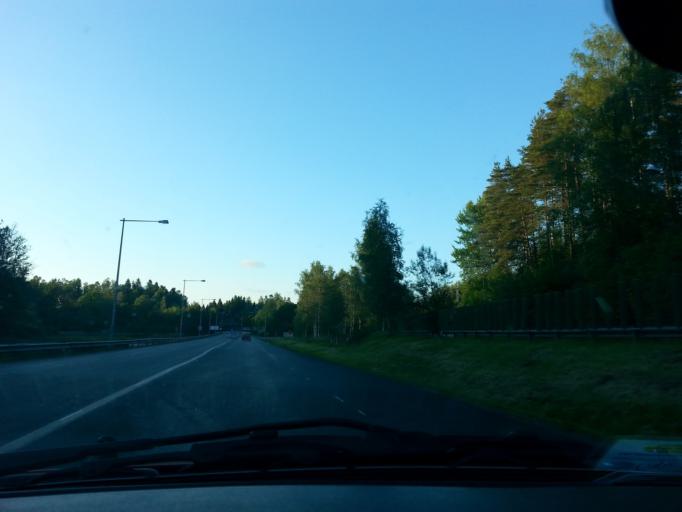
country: SE
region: Vaestra Goetaland
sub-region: Boras Kommun
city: Boras
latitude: 57.6947
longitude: 12.9474
